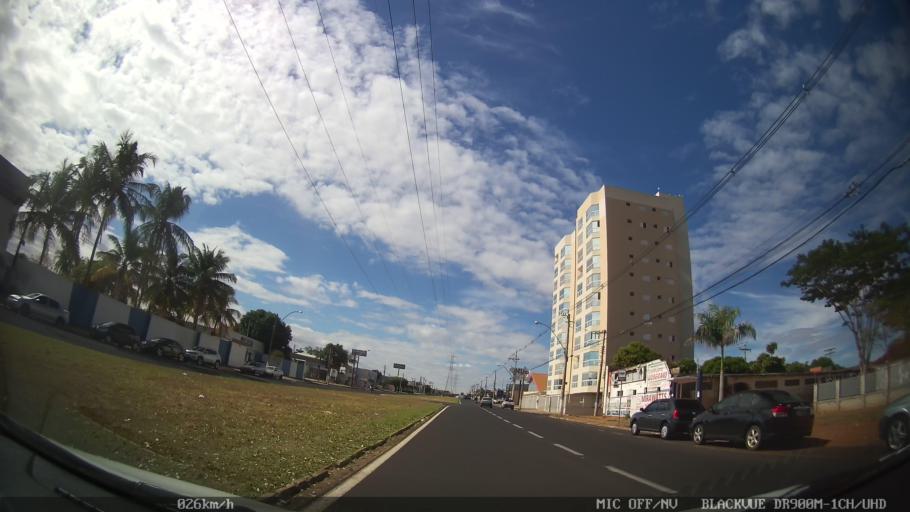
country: BR
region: Sao Paulo
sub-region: Bady Bassitt
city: Bady Bassitt
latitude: -20.8125
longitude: -49.5060
